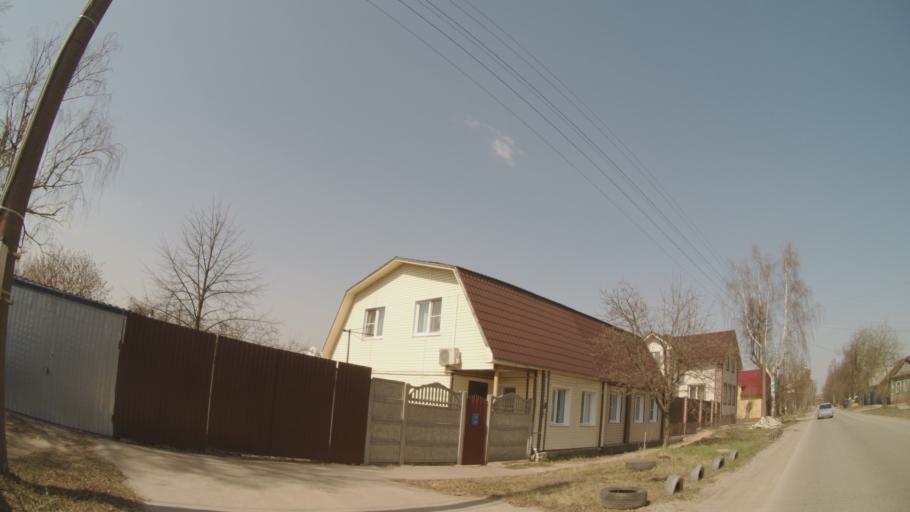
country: RU
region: Nizjnij Novgorod
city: Arzamas
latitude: 55.3900
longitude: 43.8253
